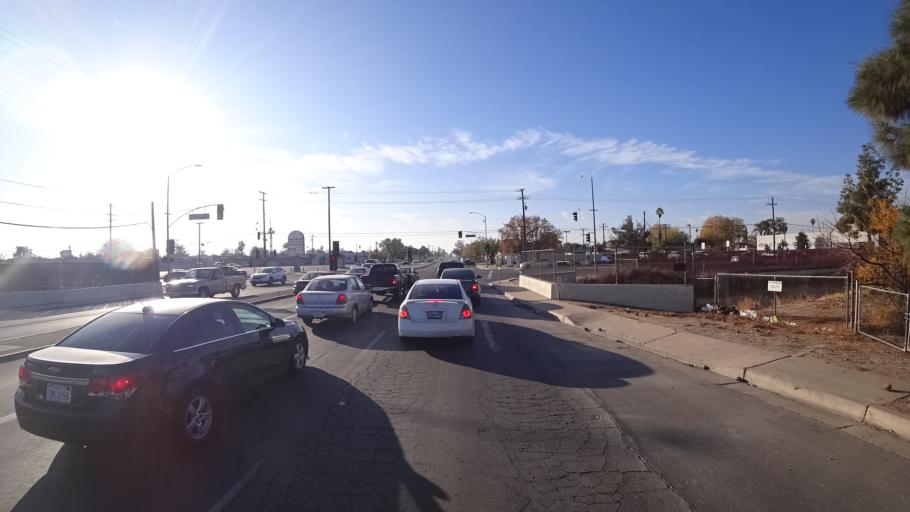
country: US
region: California
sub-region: Kern County
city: Bakersfield
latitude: 35.3395
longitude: -119.0208
